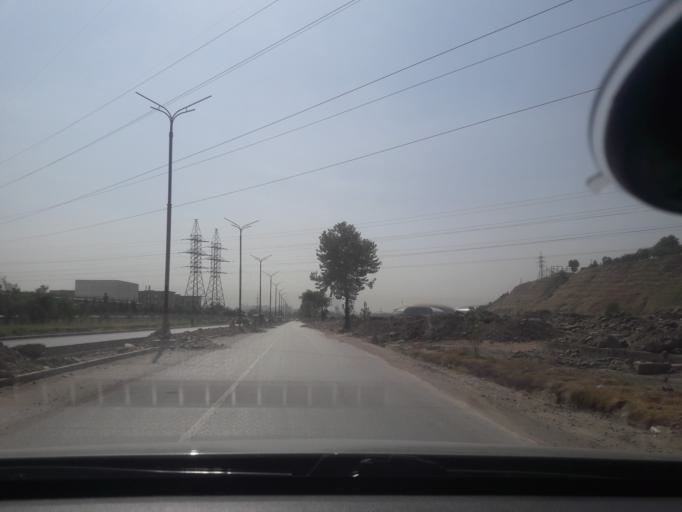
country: TJ
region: Dushanbe
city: Dushanbe
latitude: 38.6097
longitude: 68.7709
